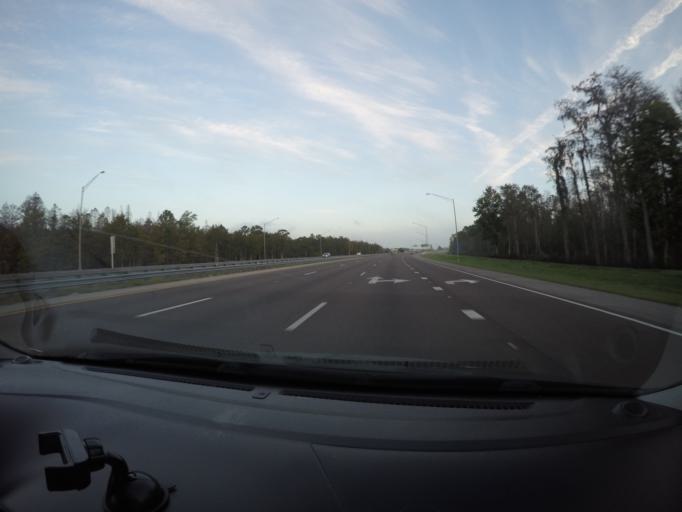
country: US
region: Florida
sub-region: Orange County
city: Azalea Park
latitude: 28.4700
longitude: -81.2372
